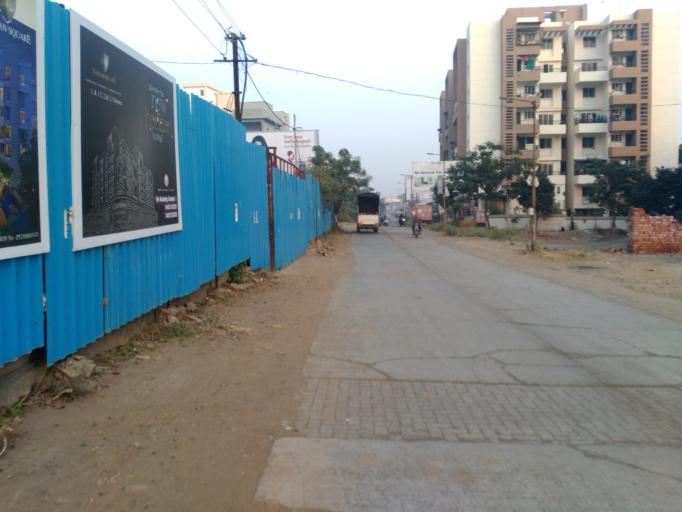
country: IN
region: Maharashtra
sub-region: Pune Division
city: Pune
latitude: 18.4391
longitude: 73.8876
